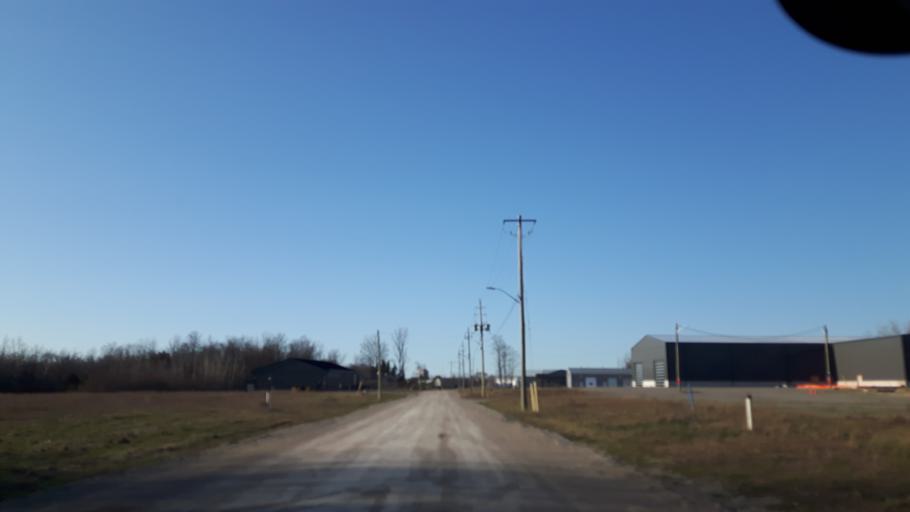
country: CA
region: Ontario
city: Goderich
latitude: 43.7255
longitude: -81.6933
